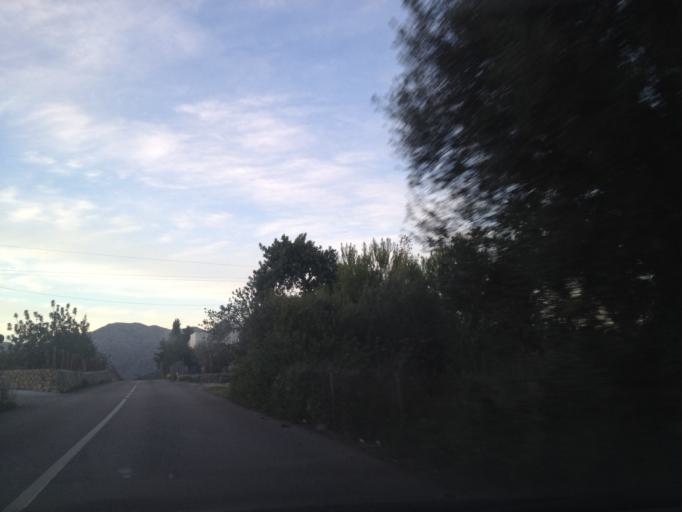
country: ES
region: Balearic Islands
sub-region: Illes Balears
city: Pollenca
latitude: 39.8658
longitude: 3.0421
